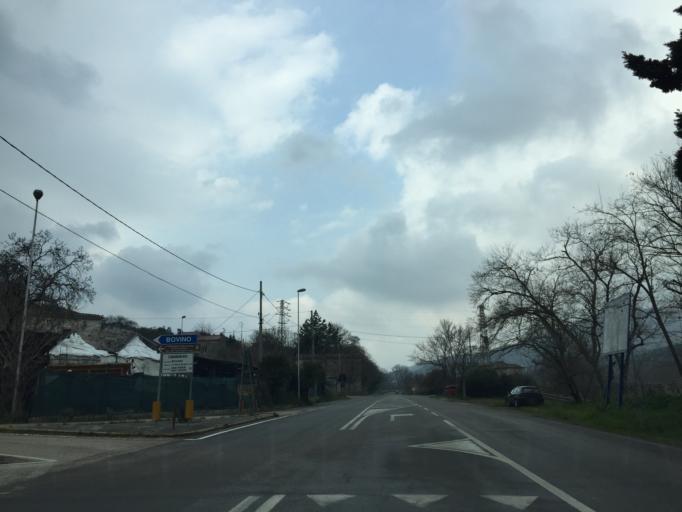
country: IT
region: Apulia
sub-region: Provincia di Foggia
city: Bovino
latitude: 41.2741
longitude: 15.3670
